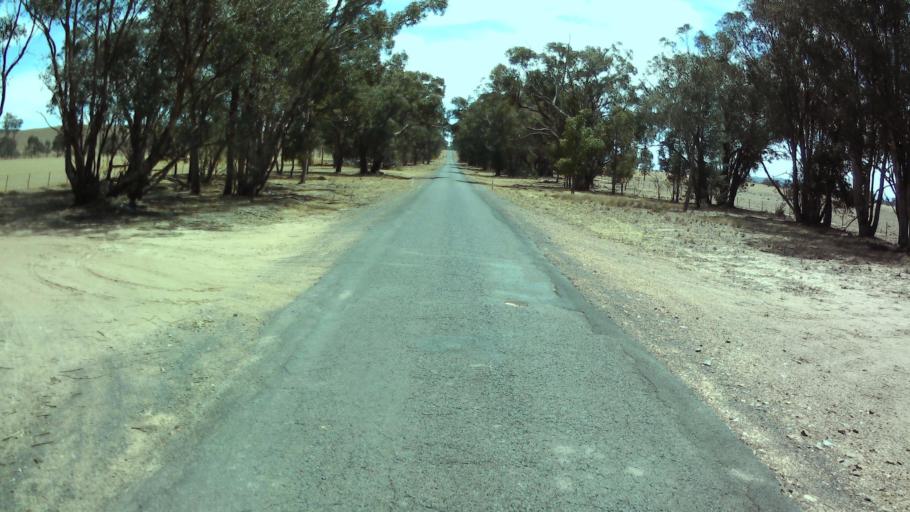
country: AU
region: New South Wales
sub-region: Weddin
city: Grenfell
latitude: -33.7654
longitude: 148.2043
